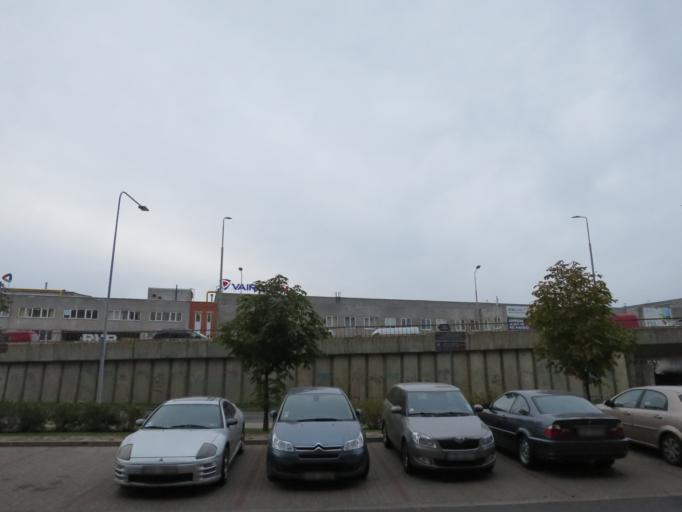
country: LV
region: Riga
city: Jaunciems
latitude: 56.9771
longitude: 24.1647
